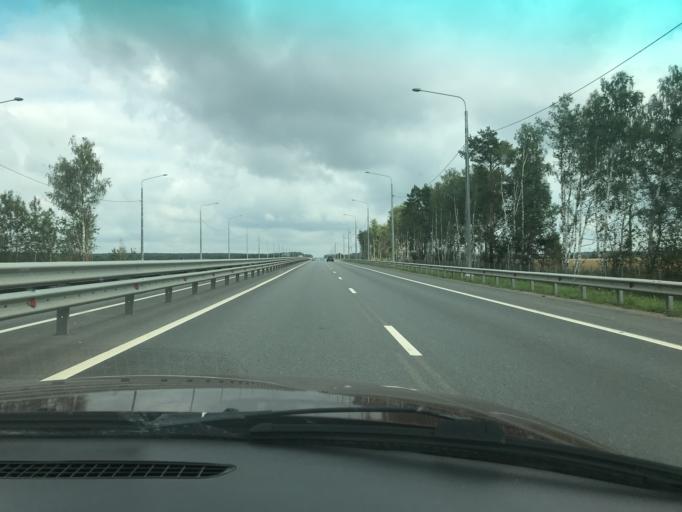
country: RU
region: Kaluga
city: Detchino
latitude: 54.7600
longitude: 36.2179
